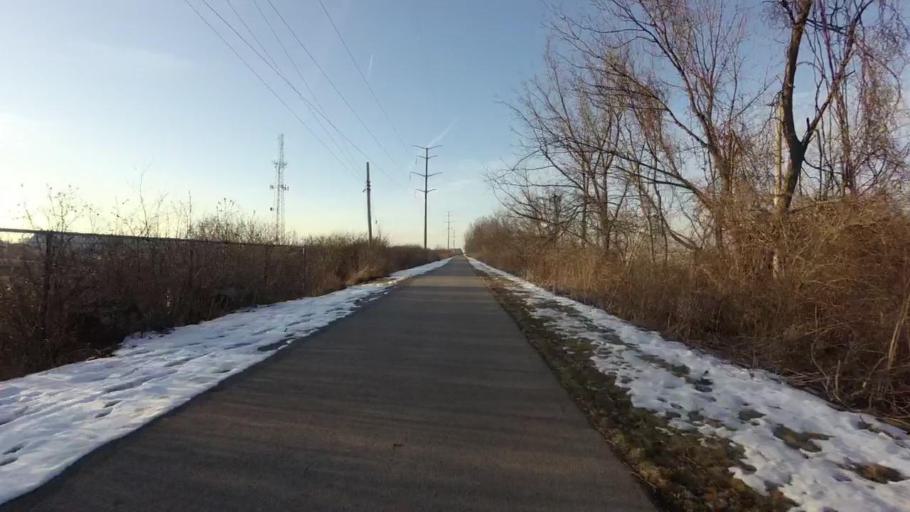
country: US
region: Wisconsin
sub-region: Milwaukee County
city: Glendale
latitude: 43.1163
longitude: -87.9275
